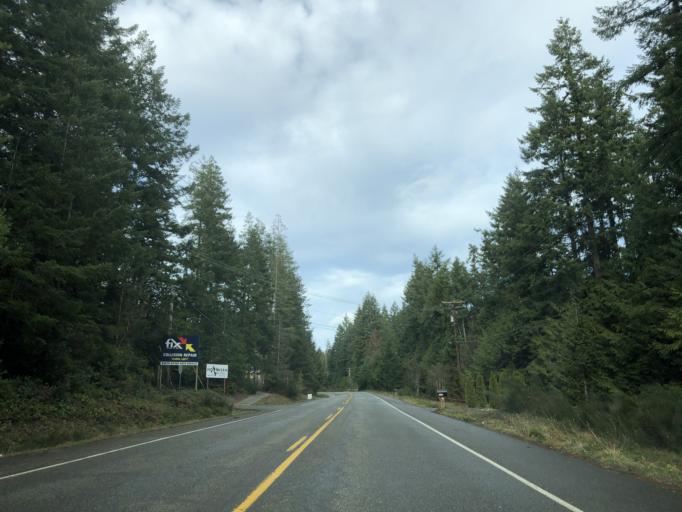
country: US
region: Washington
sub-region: Kitsap County
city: Poulsbo
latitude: 47.7629
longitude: -122.6509
